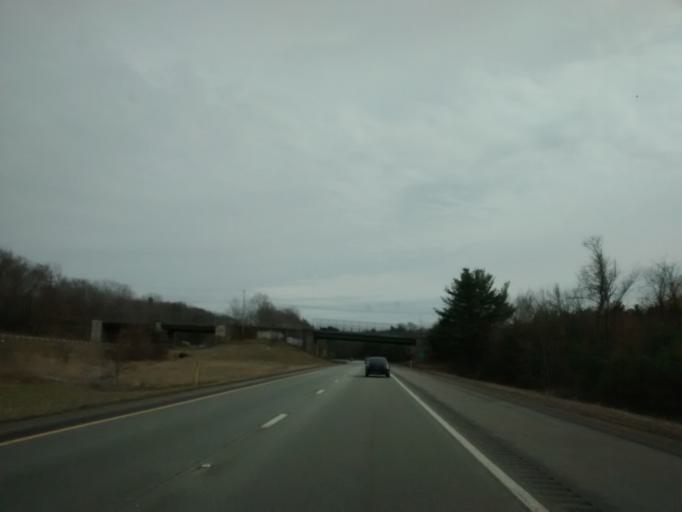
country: US
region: Massachusetts
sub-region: Worcester County
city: East Douglas
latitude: 42.0775
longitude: -71.6845
